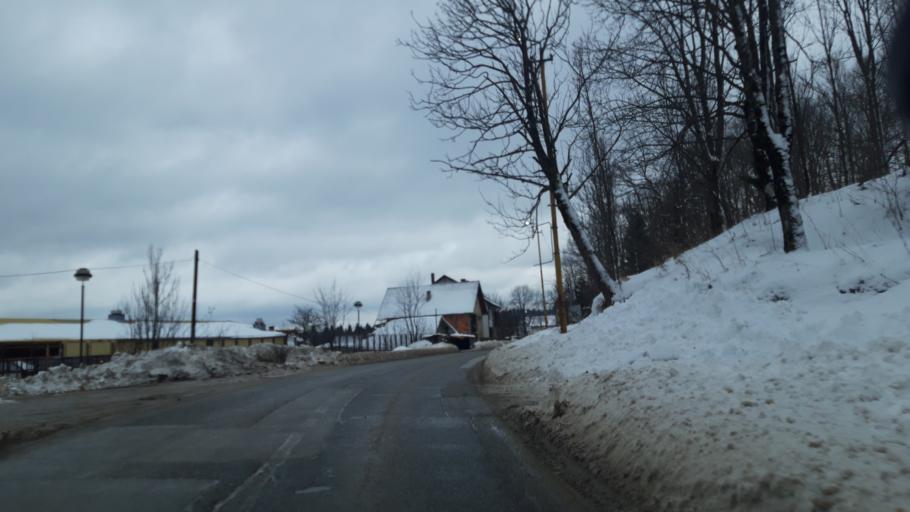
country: BA
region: Republika Srpska
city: Han Pijesak
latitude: 44.0845
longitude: 18.9543
